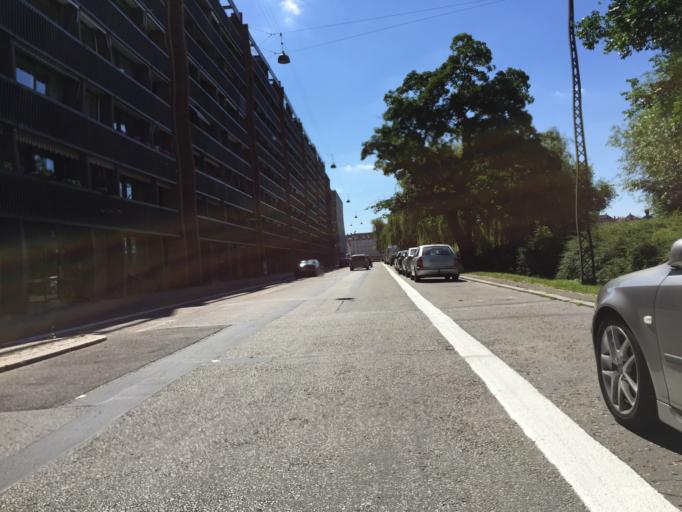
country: DK
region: Capital Region
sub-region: Kobenhavn
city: Copenhagen
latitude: 55.6776
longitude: 12.5595
